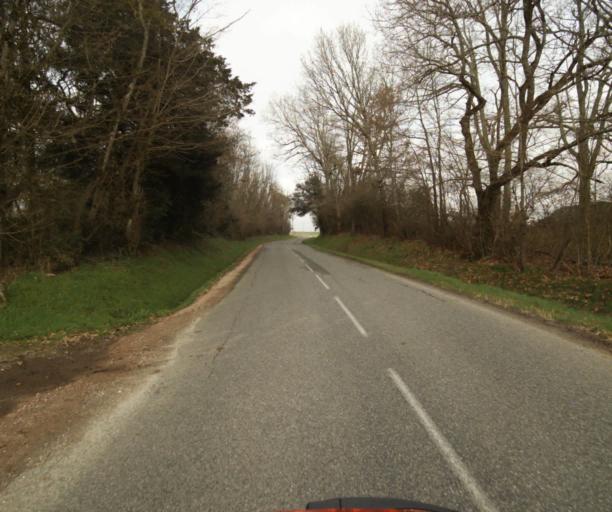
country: FR
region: Midi-Pyrenees
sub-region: Departement de l'Ariege
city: Pamiers
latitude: 43.1109
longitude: 1.5473
